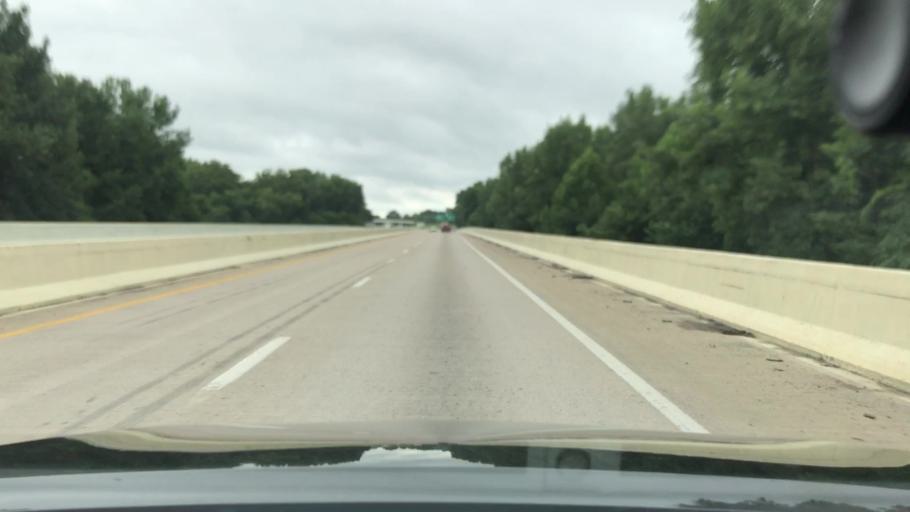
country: US
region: Ohio
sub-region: Ross County
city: Chillicothe
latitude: 39.3078
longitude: -82.9223
